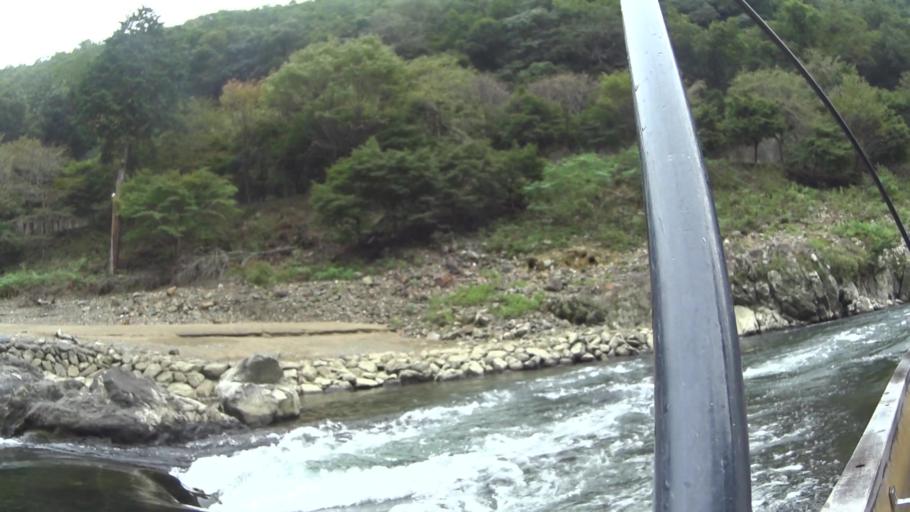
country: JP
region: Kyoto
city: Kameoka
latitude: 35.0251
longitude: 135.6550
